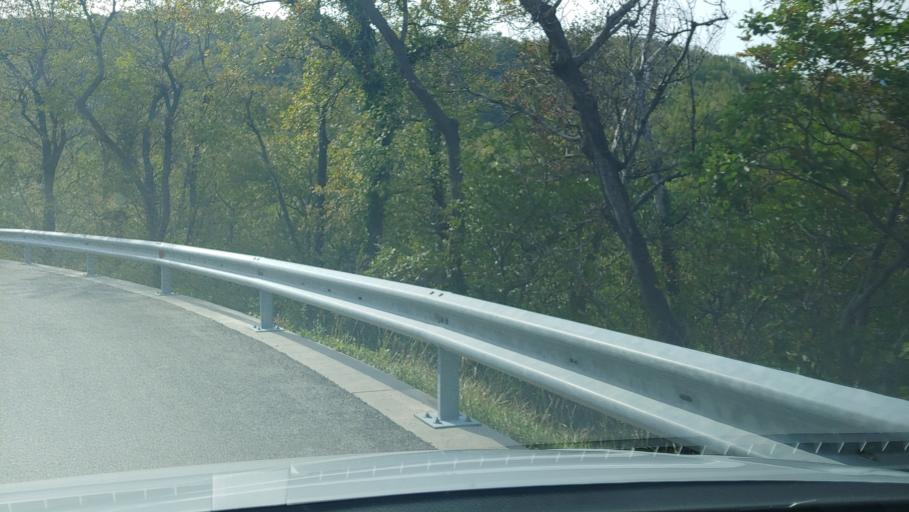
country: SI
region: Ajdovscina
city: Ajdovscina
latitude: 45.9018
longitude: 13.9082
